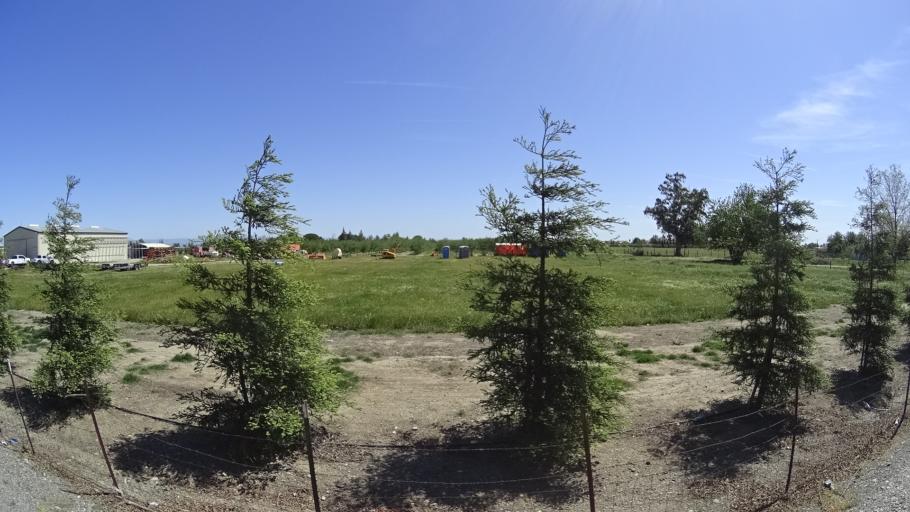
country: US
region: California
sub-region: Glenn County
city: Orland
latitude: 39.7367
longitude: -122.1781
